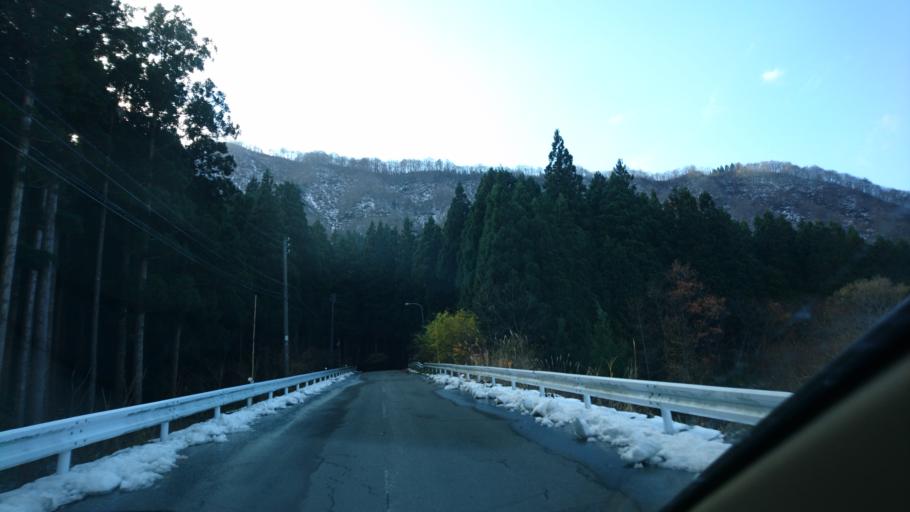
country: JP
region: Iwate
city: Kitakami
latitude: 39.2901
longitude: 140.8431
